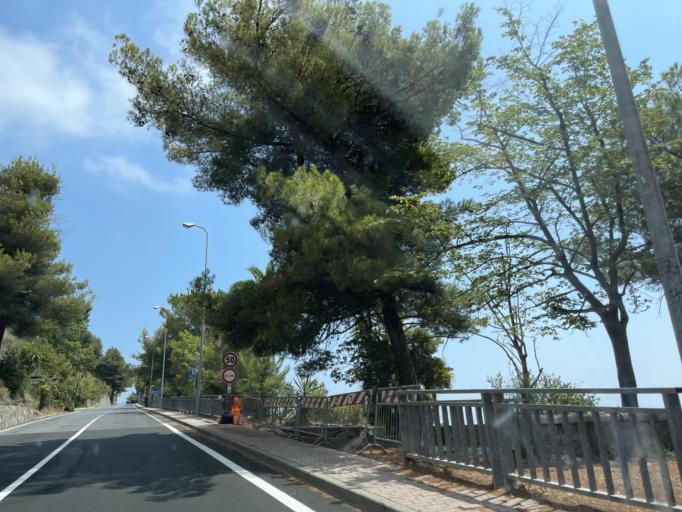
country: FR
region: Provence-Alpes-Cote d'Azur
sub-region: Departement des Alpes-Maritimes
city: Menton
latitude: 43.7857
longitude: 7.5457
